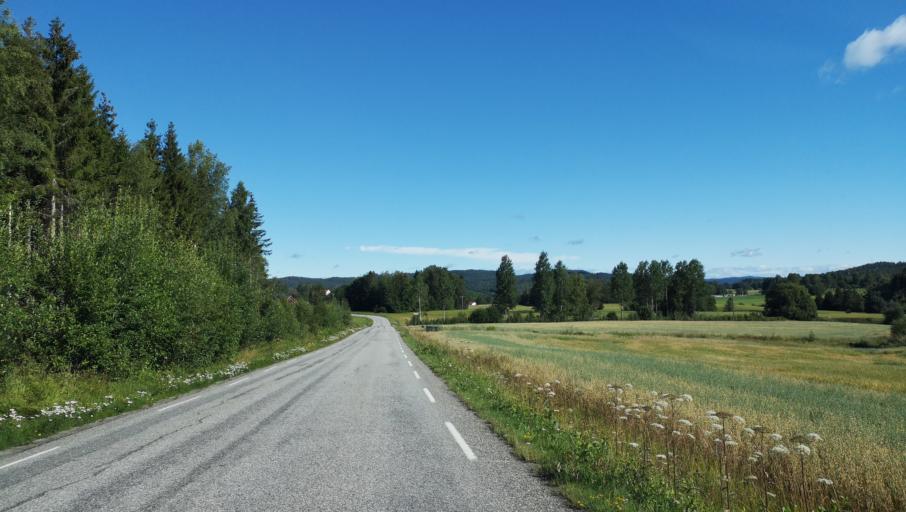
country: NO
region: Ostfold
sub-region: Hobol
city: Tomter
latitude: 59.6461
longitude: 11.0147
